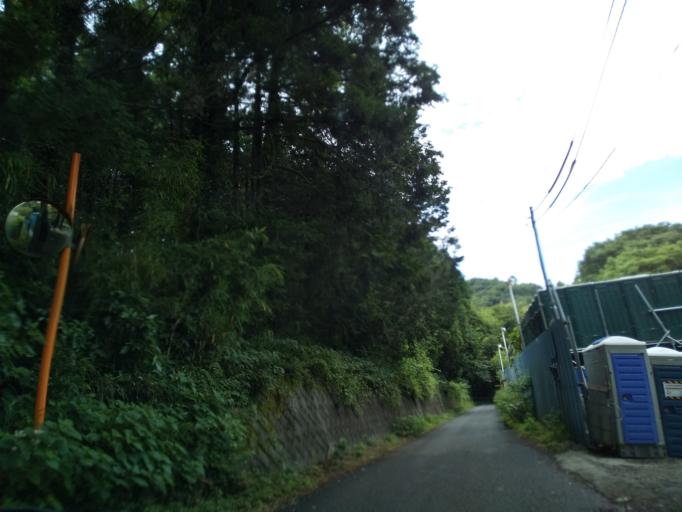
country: JP
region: Kanagawa
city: Zama
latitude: 35.5354
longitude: 139.2903
